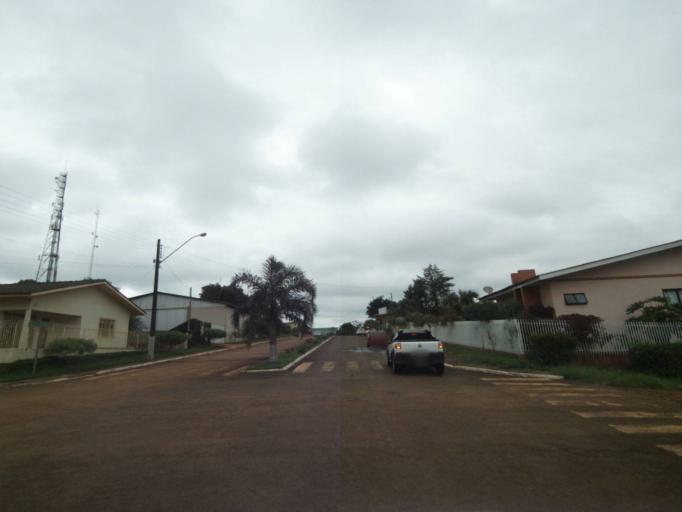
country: BR
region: Parana
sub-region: Pitanga
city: Pitanga
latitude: -24.9397
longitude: -51.8727
